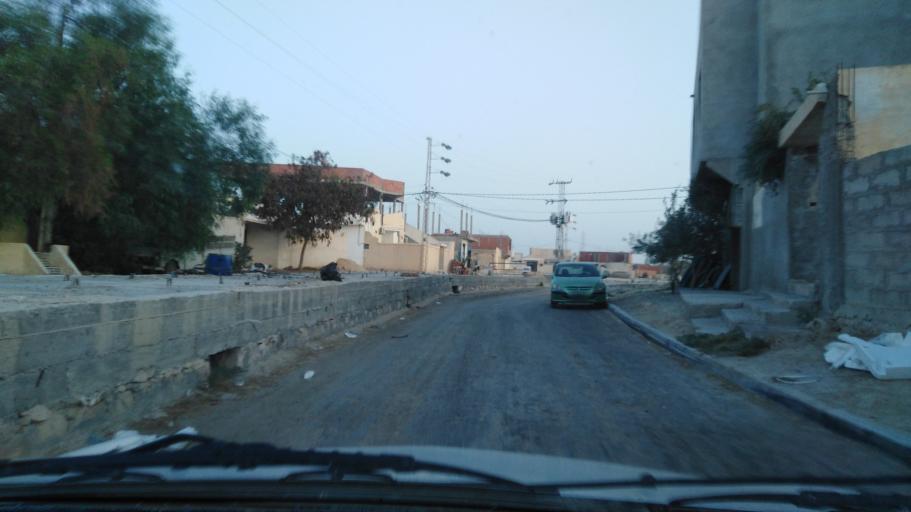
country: TN
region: Qabis
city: Gabes
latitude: 33.9561
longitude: 9.9952
